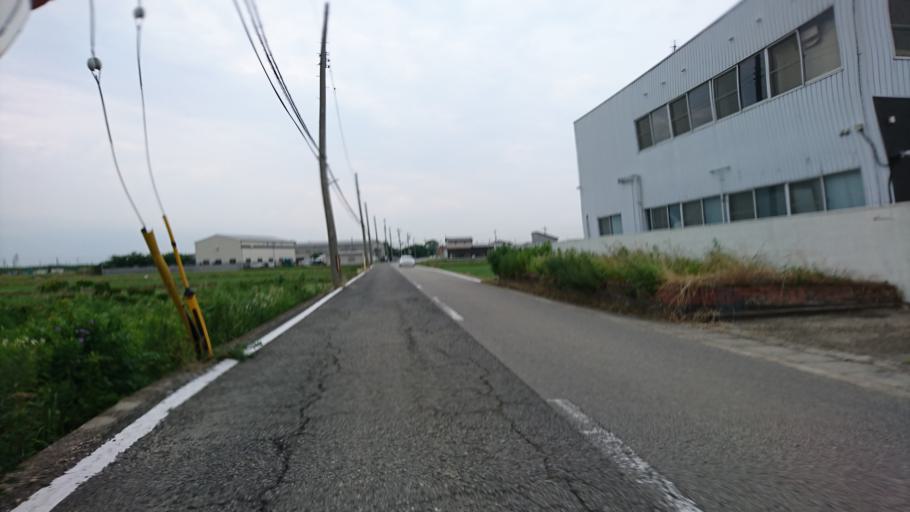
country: JP
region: Hyogo
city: Miki
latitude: 34.7355
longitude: 134.9309
